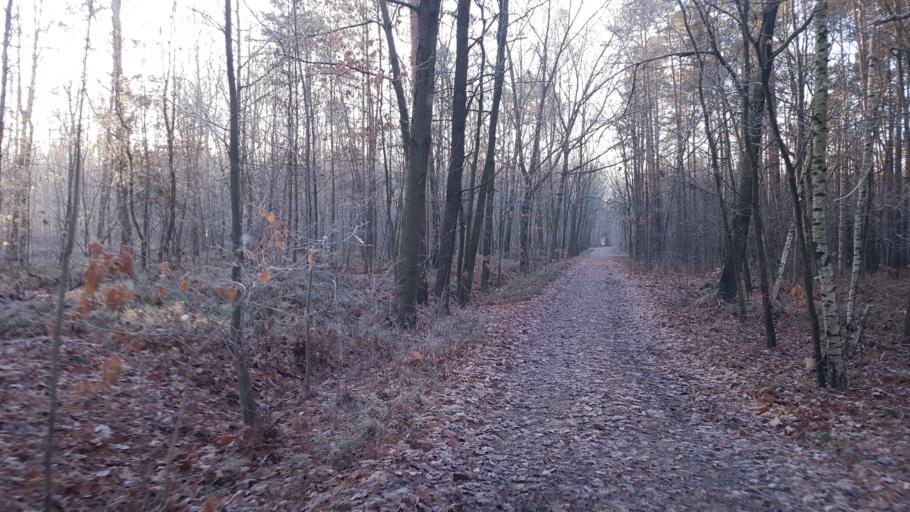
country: DE
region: Brandenburg
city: Sallgast
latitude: 51.5993
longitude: 13.8368
